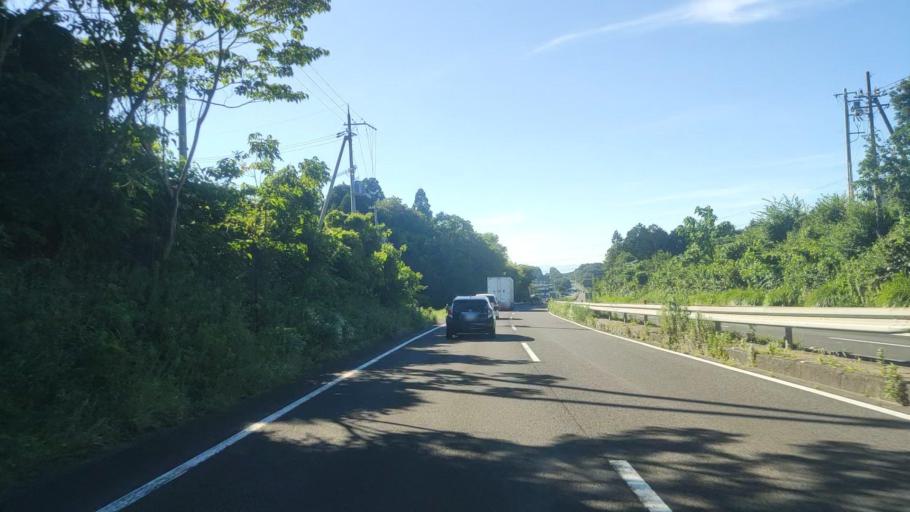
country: JP
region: Shiga Prefecture
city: Minakuchicho-matoba
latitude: 34.9622
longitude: 136.2001
